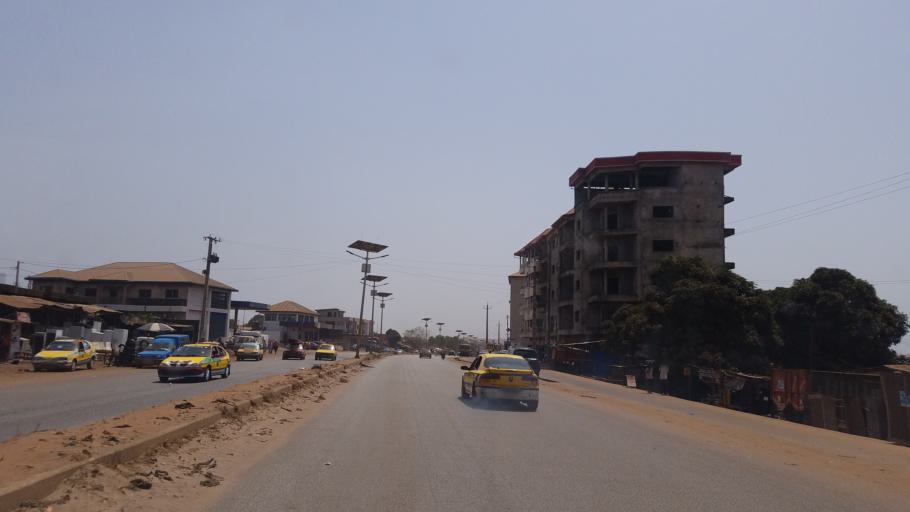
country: GN
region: Kindia
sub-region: Prefecture de Dubreka
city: Dubreka
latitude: 9.6635
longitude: -13.5635
